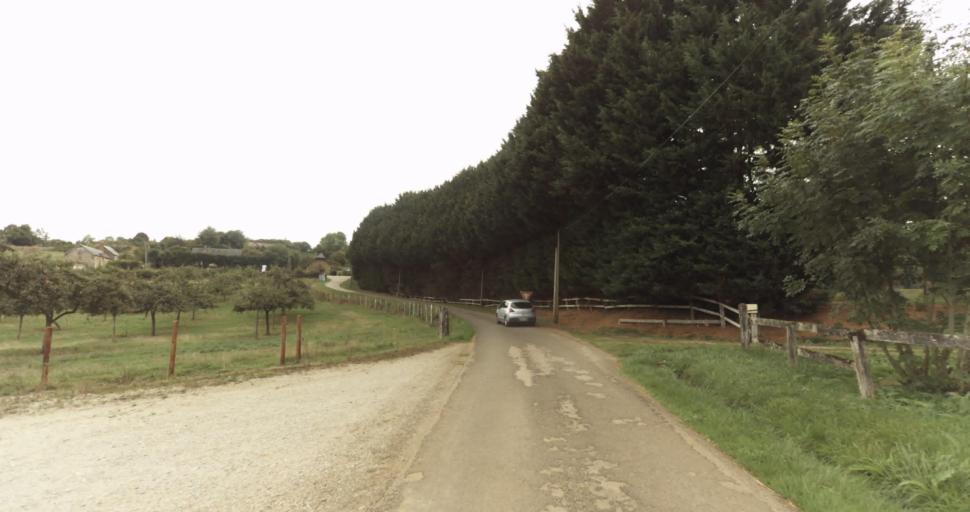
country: FR
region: Lower Normandy
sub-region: Departement de l'Orne
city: Gace
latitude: 48.7593
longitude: 0.3377
